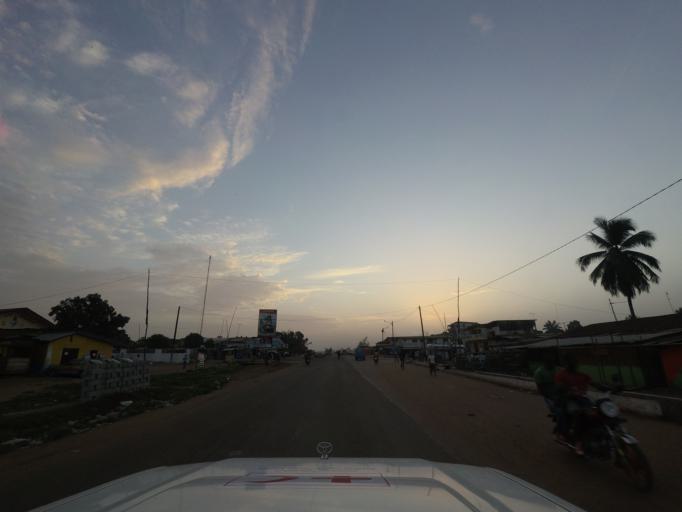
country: LR
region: Montserrado
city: Monrovia
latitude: 6.2966
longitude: -10.6838
